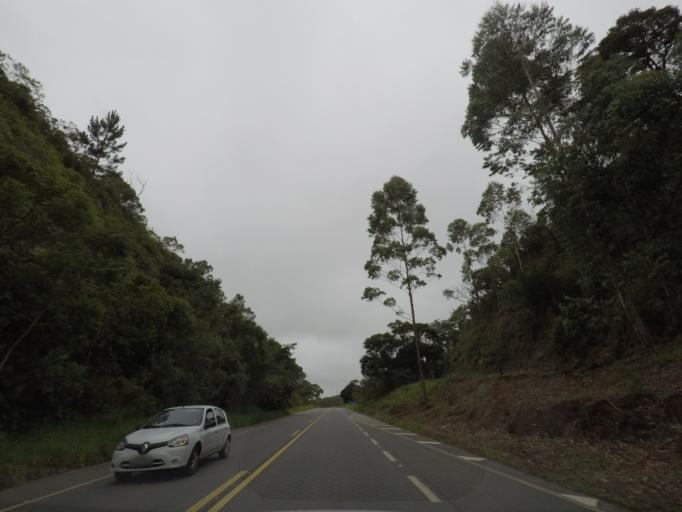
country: BR
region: Sao Paulo
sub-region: Guaratingueta
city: Guaratingueta
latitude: -22.9308
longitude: -45.0770
